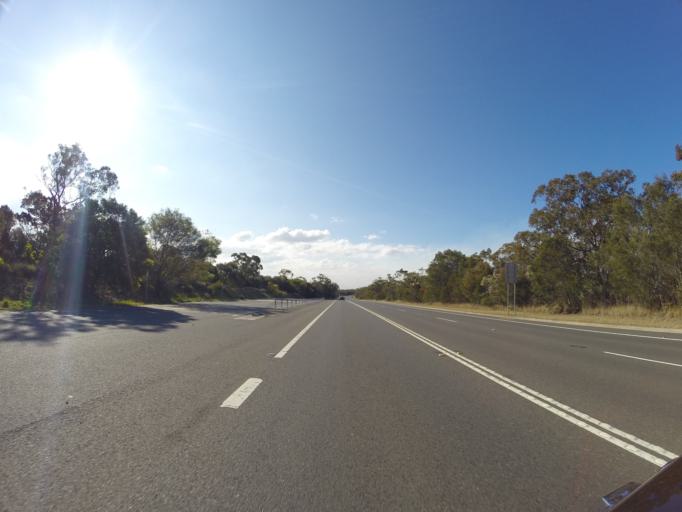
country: AU
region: New South Wales
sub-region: Liverpool
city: Holsworthy
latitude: -34.0378
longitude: 150.9600
